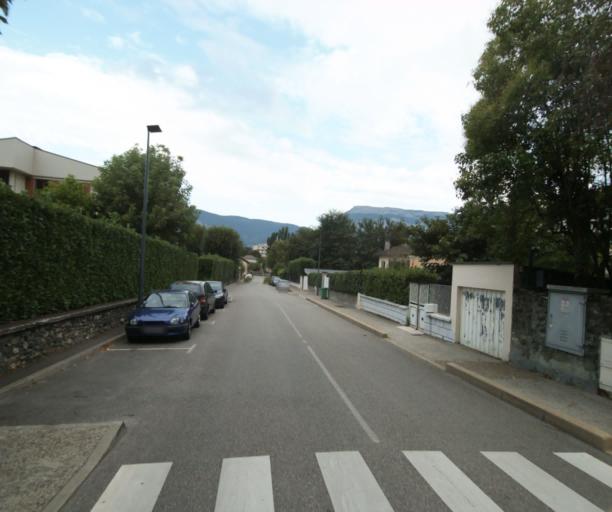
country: FR
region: Rhone-Alpes
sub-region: Departement de l'Isere
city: Gieres
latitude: 45.1800
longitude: 5.7894
